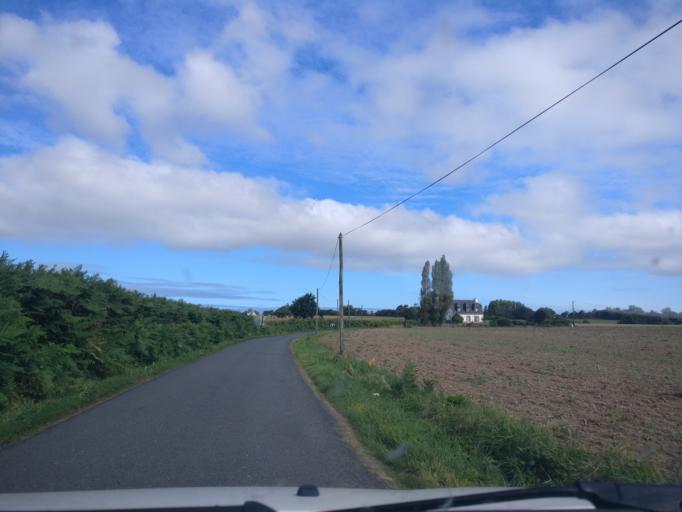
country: FR
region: Brittany
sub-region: Departement des Cotes-d'Armor
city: Rospez
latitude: 48.7464
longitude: -3.3742
